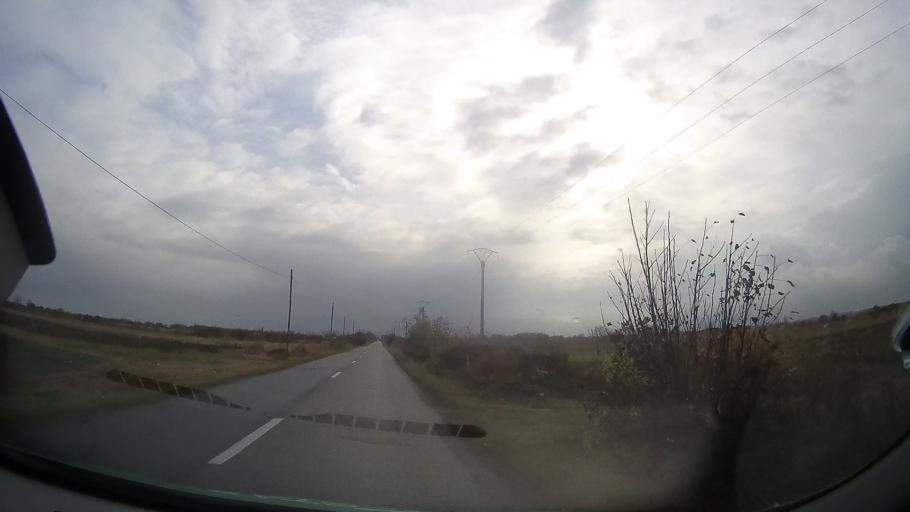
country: RO
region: Ialomita
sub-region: Comuna Fierbinti-Targ
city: Fierbintii de Jos
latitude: 44.7075
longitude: 26.3920
